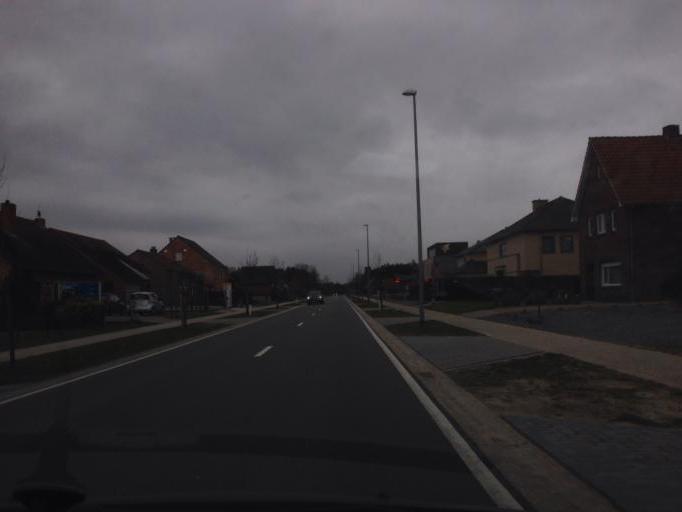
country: BE
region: Flanders
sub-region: Provincie Limburg
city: Bree
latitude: 51.1153
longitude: 5.5527
